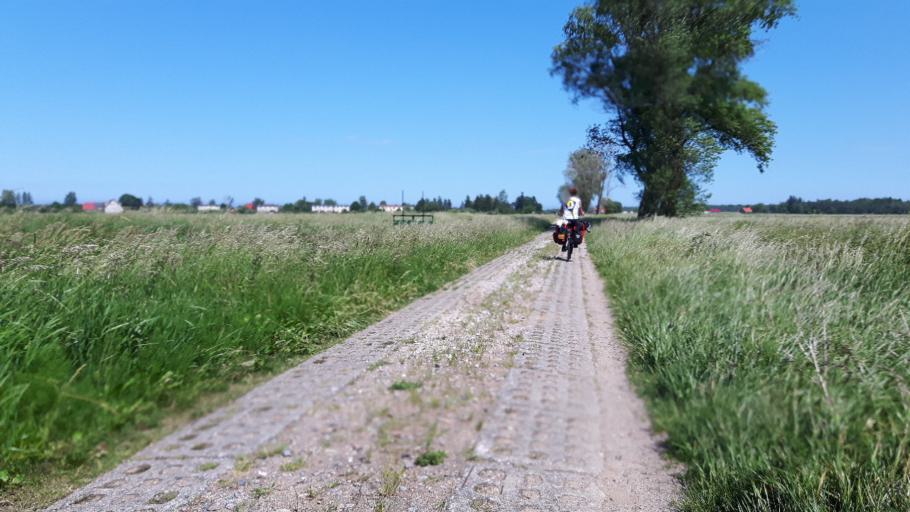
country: PL
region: Pomeranian Voivodeship
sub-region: Powiat slupski
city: Smoldzino
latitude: 54.6819
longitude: 17.2758
